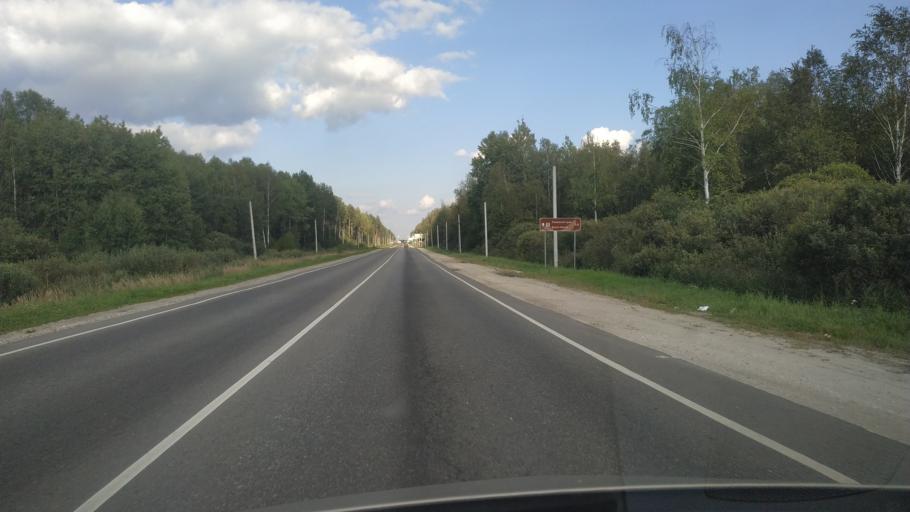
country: RU
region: Moskovskaya
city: Shaturtorf
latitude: 55.5778
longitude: 39.4298
